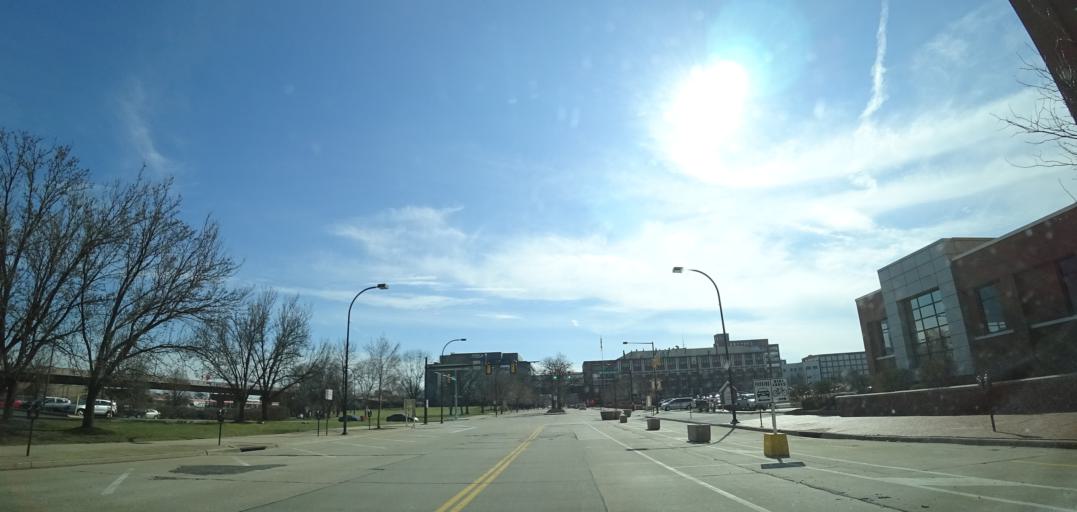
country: US
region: Ohio
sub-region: Summit County
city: Akron
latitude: 41.0741
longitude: -81.5238
